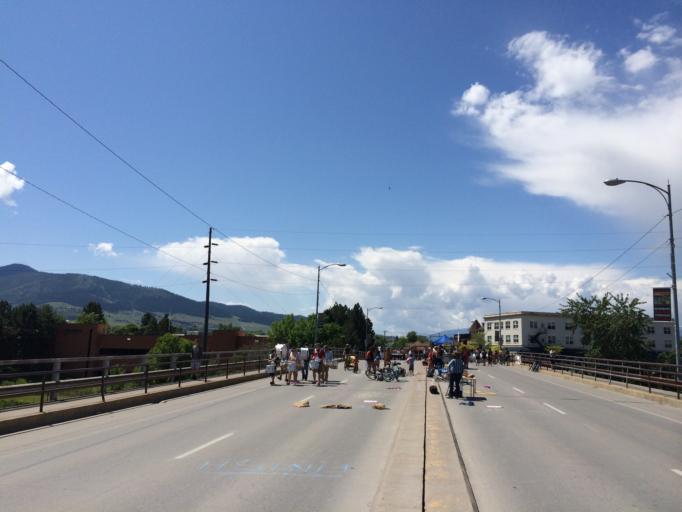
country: US
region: Montana
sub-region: Missoula County
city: Missoula
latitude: 46.8680
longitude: -113.9966
